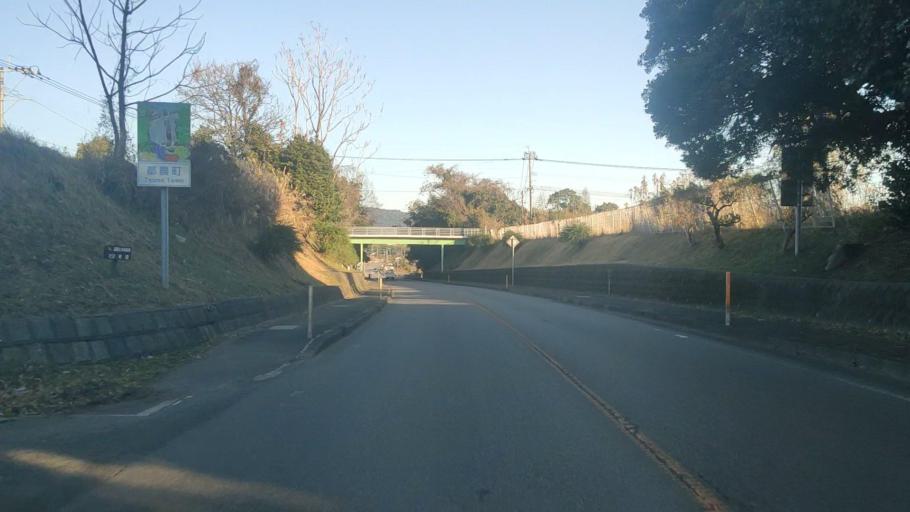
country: JP
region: Miyazaki
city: Takanabe
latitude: 32.2345
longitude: 131.5487
